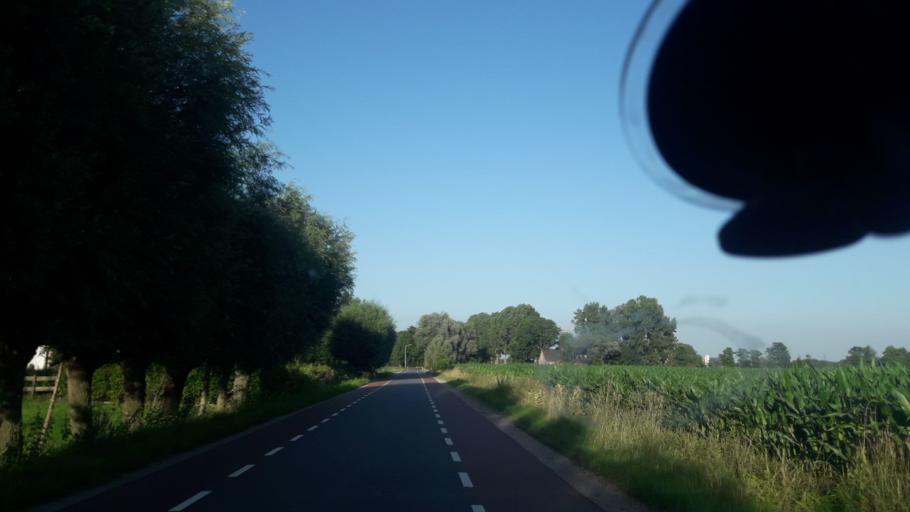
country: NL
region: Utrecht
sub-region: Gemeente Veenendaal
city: Veenendaal
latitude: 52.0136
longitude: 5.5990
